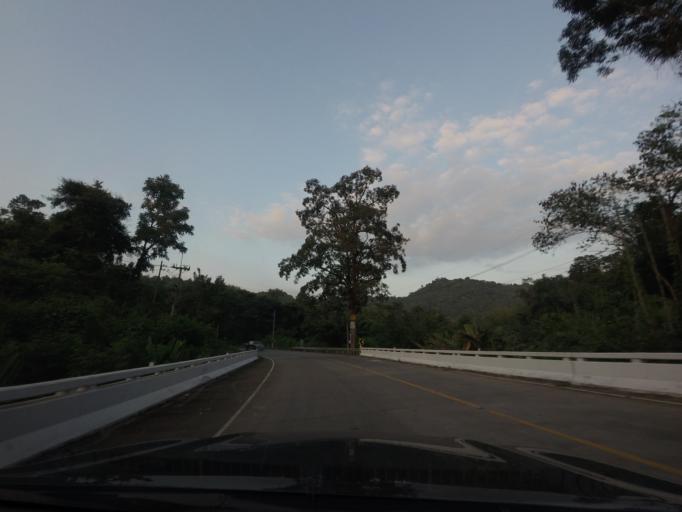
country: TH
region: Nan
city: Na Noi
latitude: 18.3841
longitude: 100.7111
